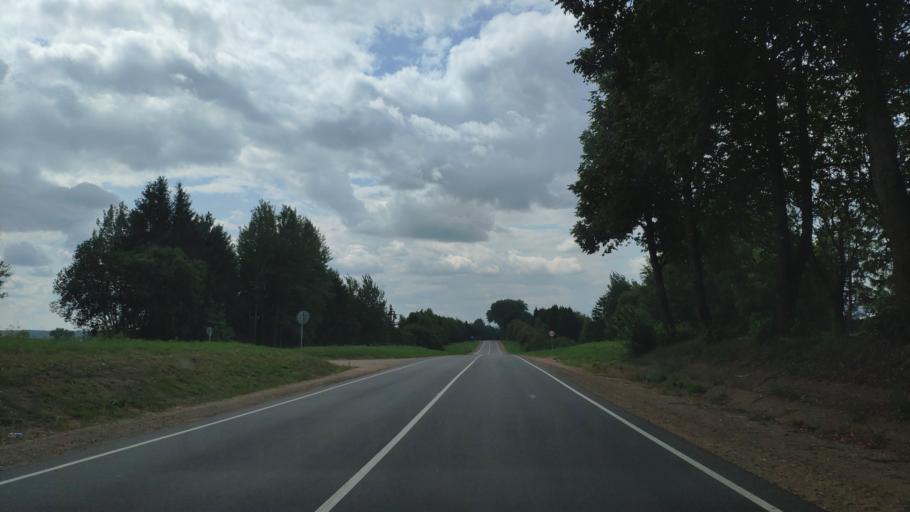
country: BY
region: Minsk
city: Syomkava
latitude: 54.0063
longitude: 27.3675
